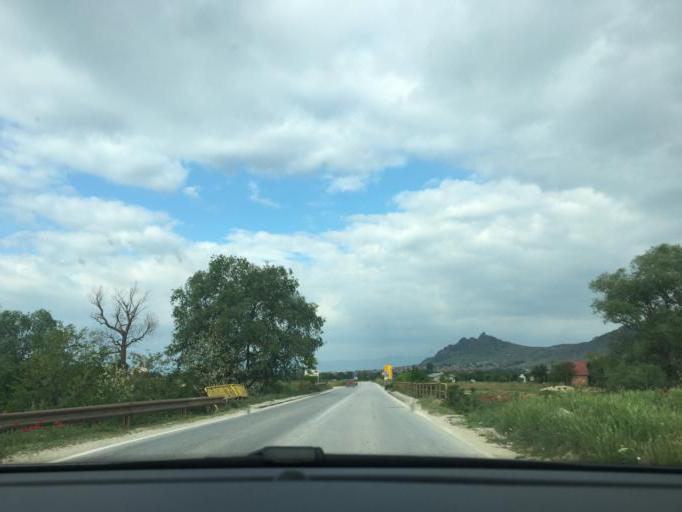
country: MK
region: Prilep
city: Prilep
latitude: 41.3593
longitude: 21.5897
